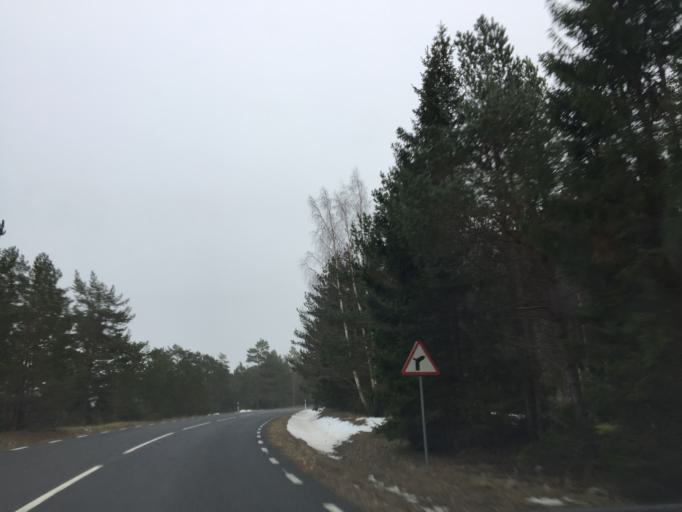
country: EE
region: Saare
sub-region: Kuressaare linn
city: Kuressaare
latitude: 58.4646
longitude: 22.0452
